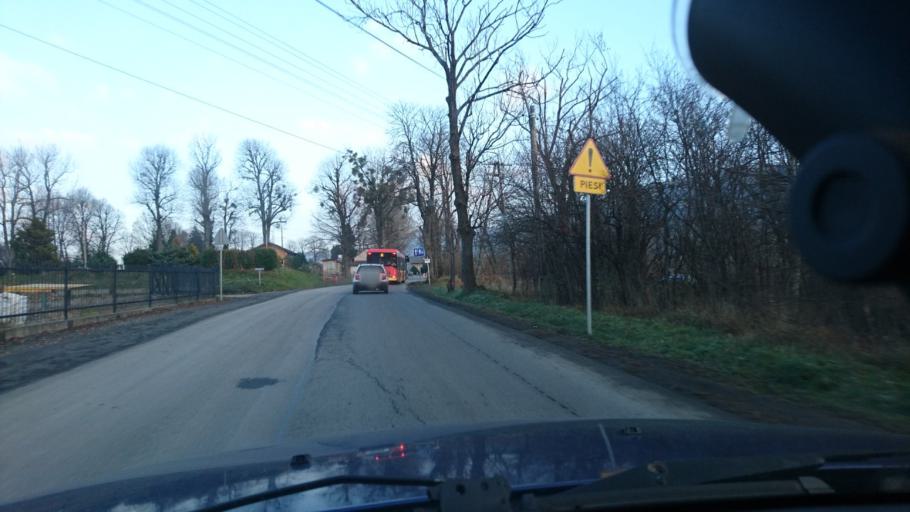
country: PL
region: Silesian Voivodeship
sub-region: Bielsko-Biala
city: Bielsko-Biala
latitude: 49.8201
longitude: 19.0901
